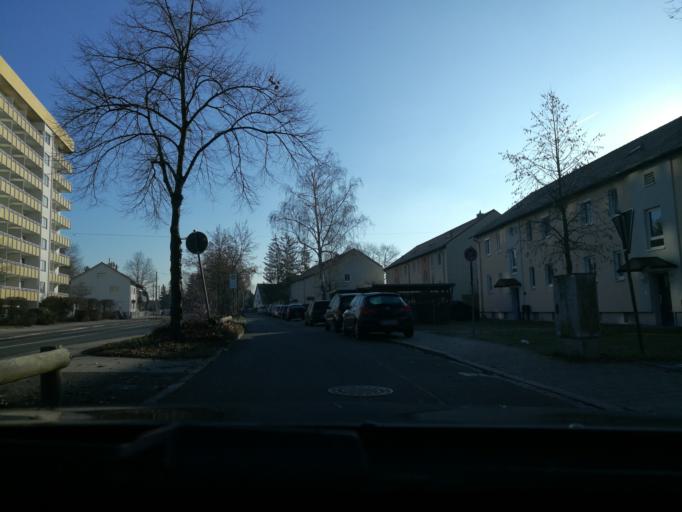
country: DE
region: Bavaria
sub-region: Regierungsbezirk Mittelfranken
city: Buckenhof
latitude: 49.5947
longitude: 11.0425
